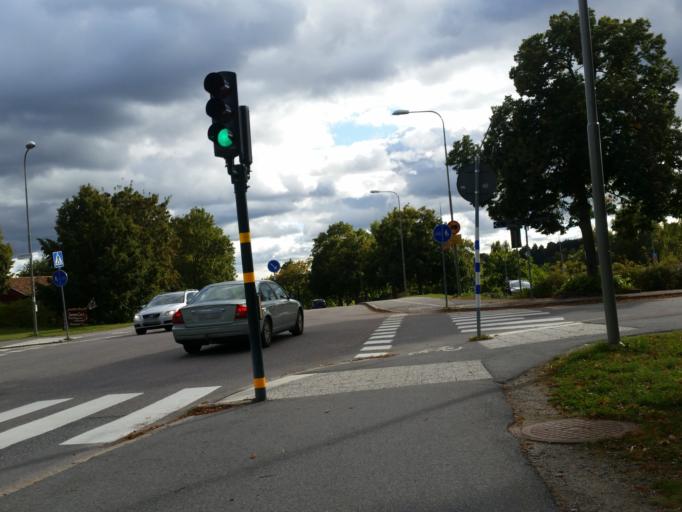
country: SE
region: Stockholm
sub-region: Stockholms Kommun
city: Arsta
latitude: 59.2730
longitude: 18.1097
